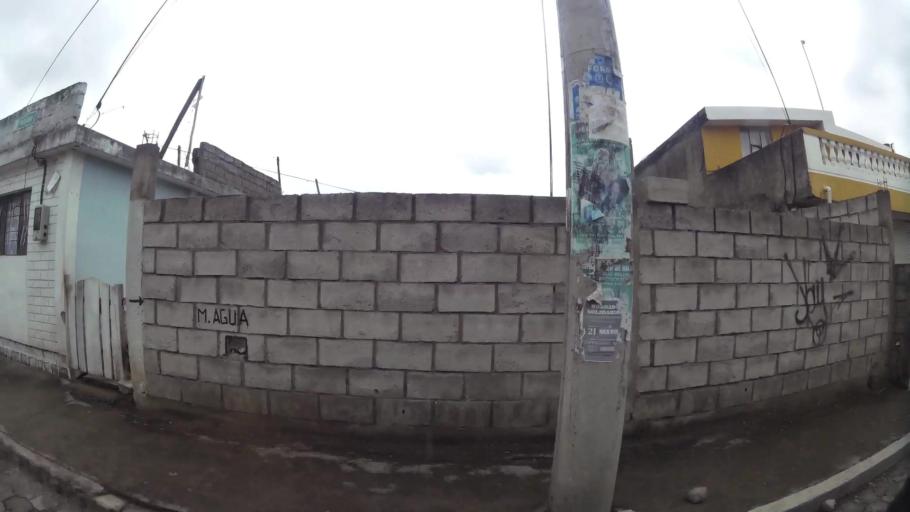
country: EC
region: Pichincha
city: Sangolqui
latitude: -0.3302
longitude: -78.4751
